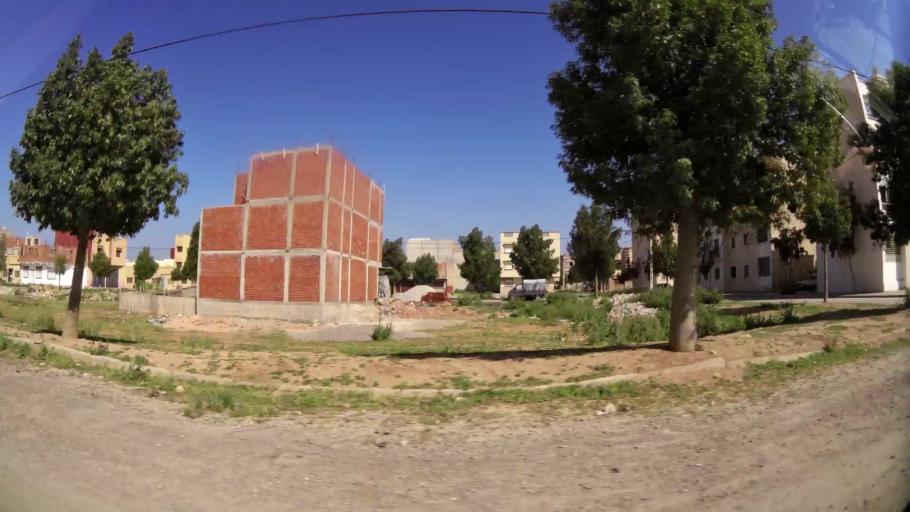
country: MA
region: Oriental
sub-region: Oujda-Angad
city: Oujda
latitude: 34.6993
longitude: -1.8801
